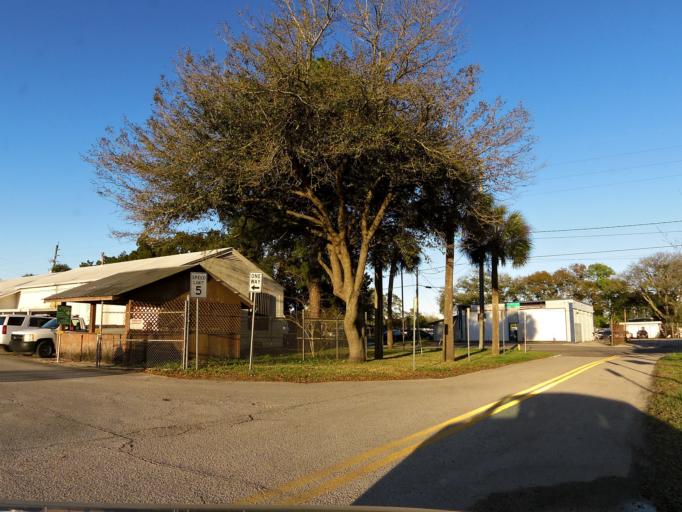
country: US
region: Florida
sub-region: Duval County
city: Jacksonville
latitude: 30.3386
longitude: -81.7103
